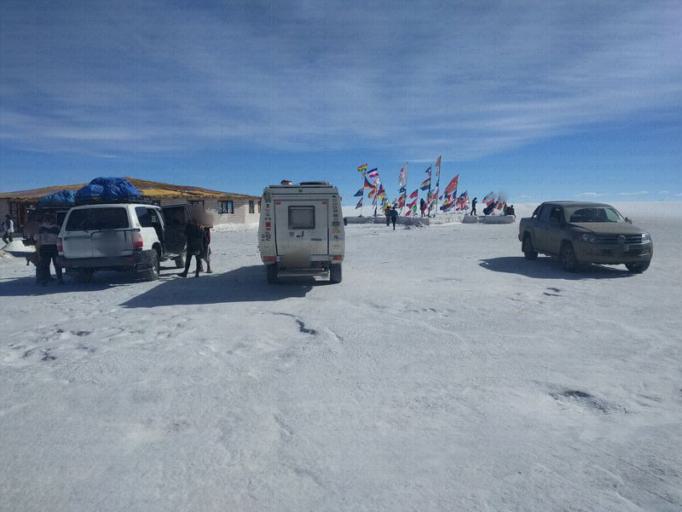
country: BO
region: Potosi
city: Colchani
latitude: -20.3302
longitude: -67.0466
